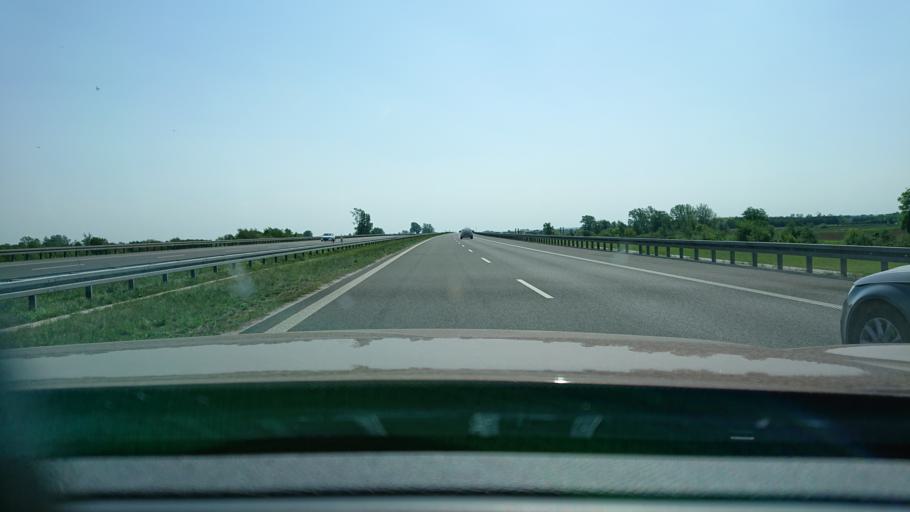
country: PL
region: Subcarpathian Voivodeship
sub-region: Powiat przeworski
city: Grzeska
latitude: 50.1102
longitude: 22.4312
